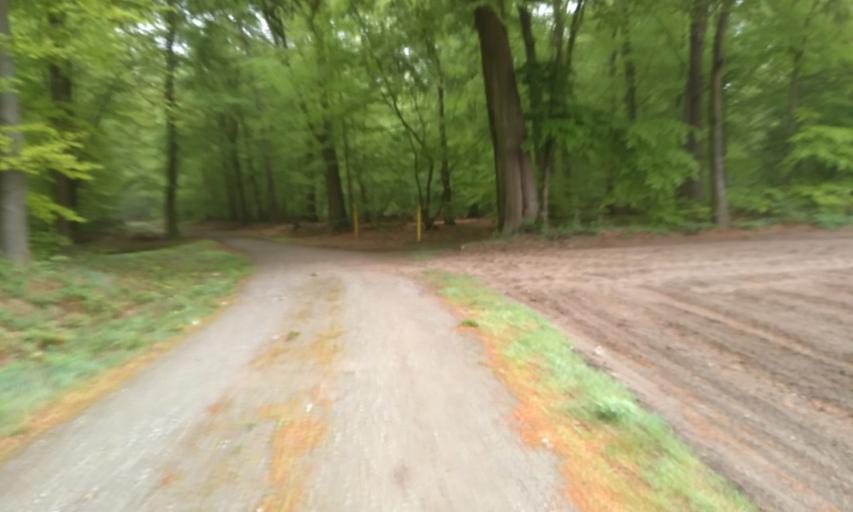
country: DE
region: Lower Saxony
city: Nottensdorf
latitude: 53.4741
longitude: 9.6344
